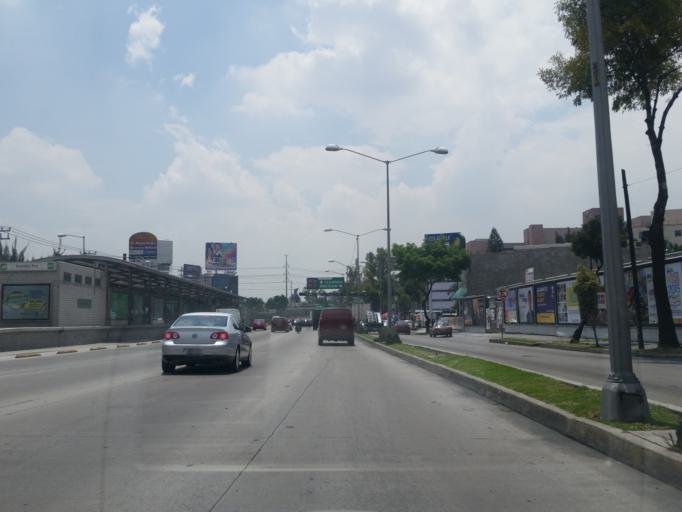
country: MX
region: Mexico City
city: Cuauhtemoc
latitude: 19.4687
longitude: -99.1443
